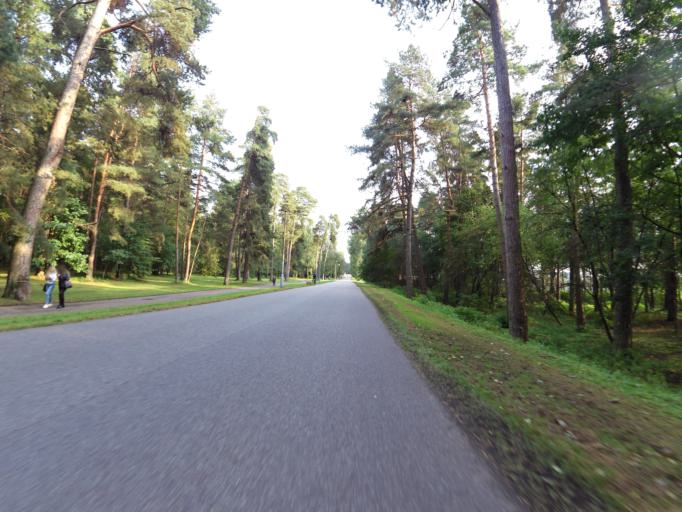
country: LT
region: Vilnius County
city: Vilkpede
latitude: 54.6769
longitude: 25.2360
